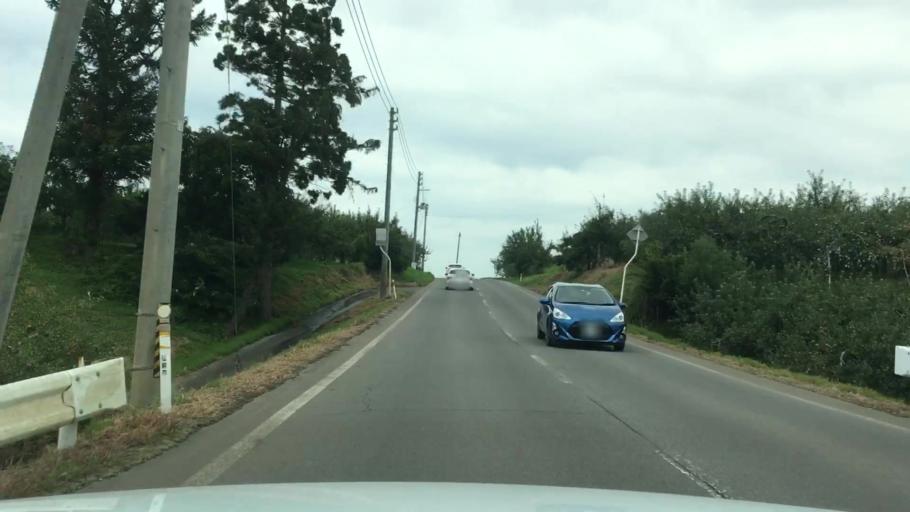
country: JP
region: Aomori
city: Hirosaki
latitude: 40.6561
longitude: 140.4204
